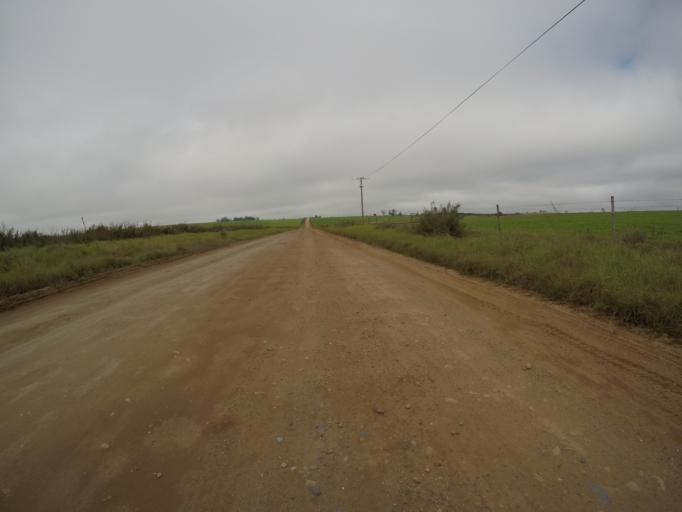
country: ZA
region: Eastern Cape
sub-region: Cacadu District Municipality
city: Kareedouw
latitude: -34.0243
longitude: 24.2410
